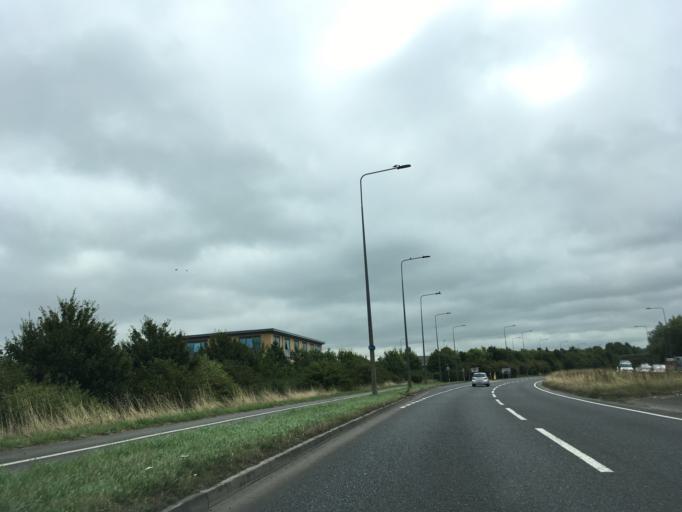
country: GB
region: England
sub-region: South Gloucestershire
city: Mangotsfield
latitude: 51.5053
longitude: -2.4887
